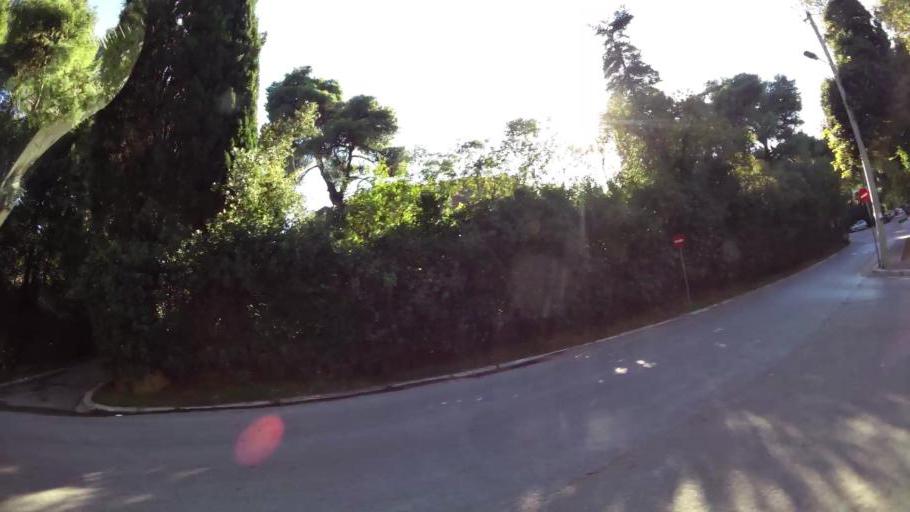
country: GR
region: Attica
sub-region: Nomarchia Athinas
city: Ekali
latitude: 38.1075
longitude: 23.8387
